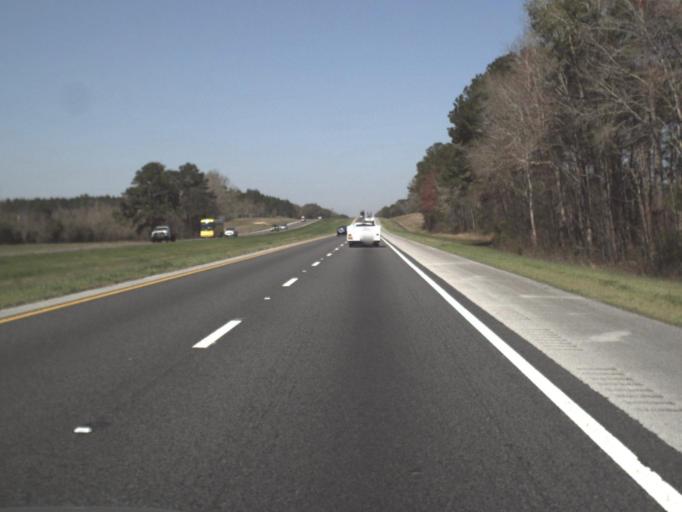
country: US
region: Florida
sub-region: Jackson County
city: Marianna
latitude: 30.6905
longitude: -85.1174
